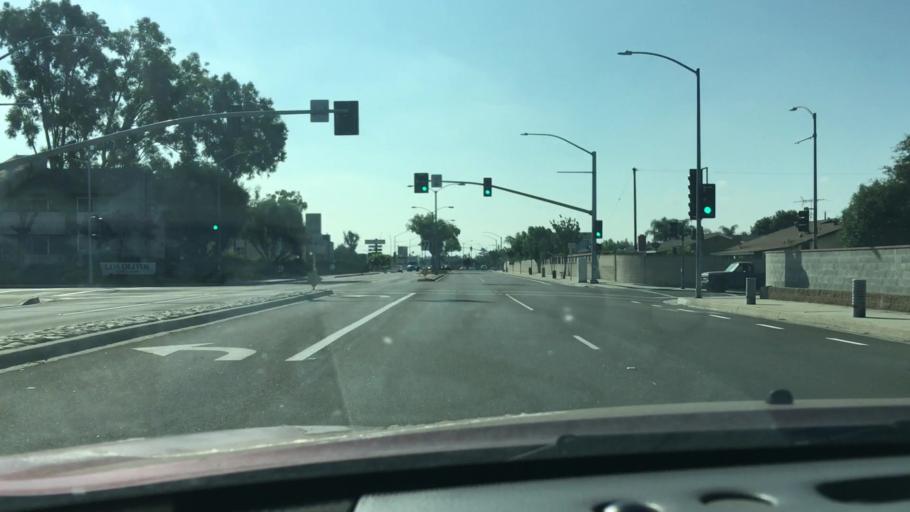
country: US
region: California
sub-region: Orange County
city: Buena Park
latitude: 33.8922
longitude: -118.0043
